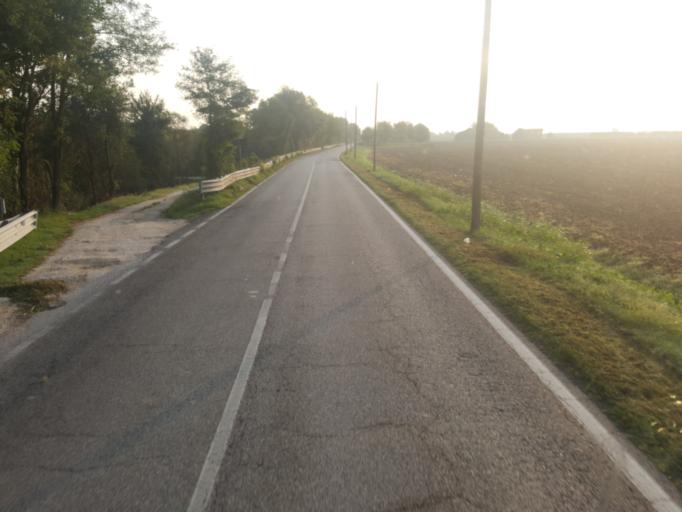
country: IT
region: Emilia-Romagna
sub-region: Provincia di Ferrara
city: San Biagio
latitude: 44.5802
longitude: 11.8855
